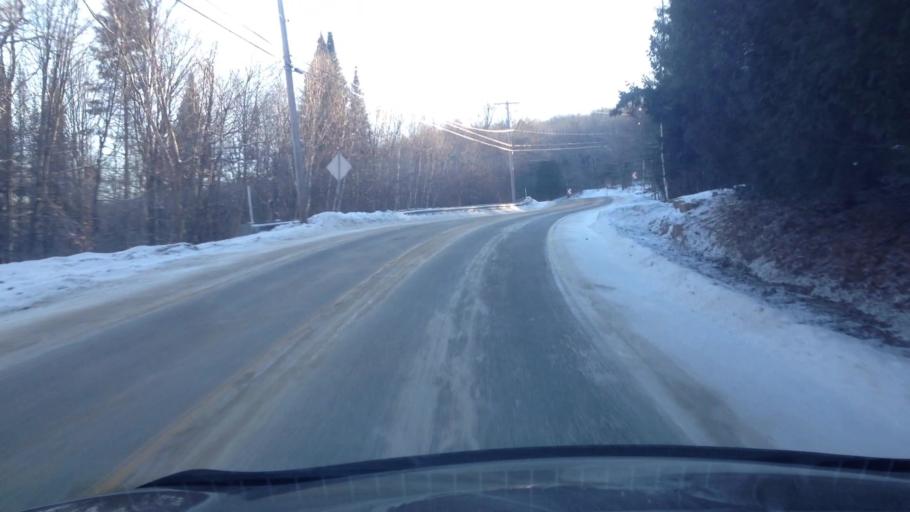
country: CA
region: Quebec
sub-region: Laurentides
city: Brownsburg-Chatham
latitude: 45.9225
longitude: -74.5093
